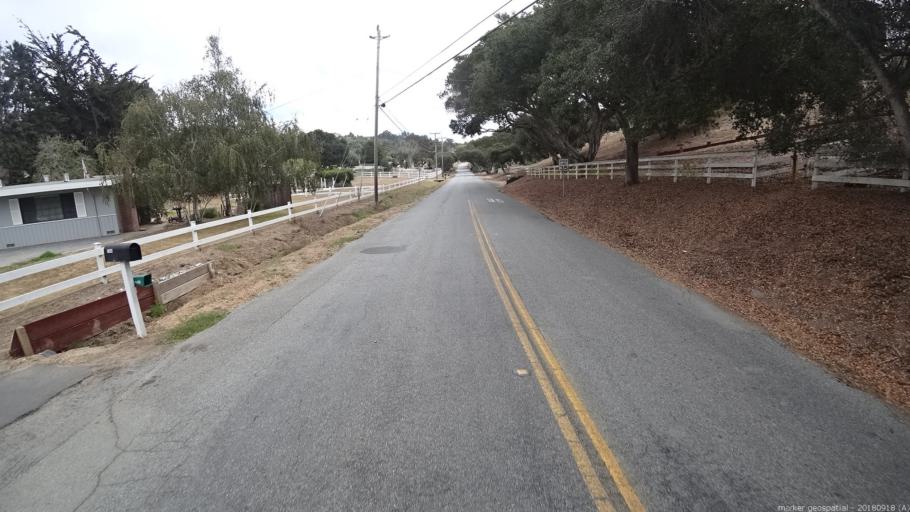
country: US
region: California
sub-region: Monterey County
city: Prunedale
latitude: 36.7905
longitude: -121.6605
